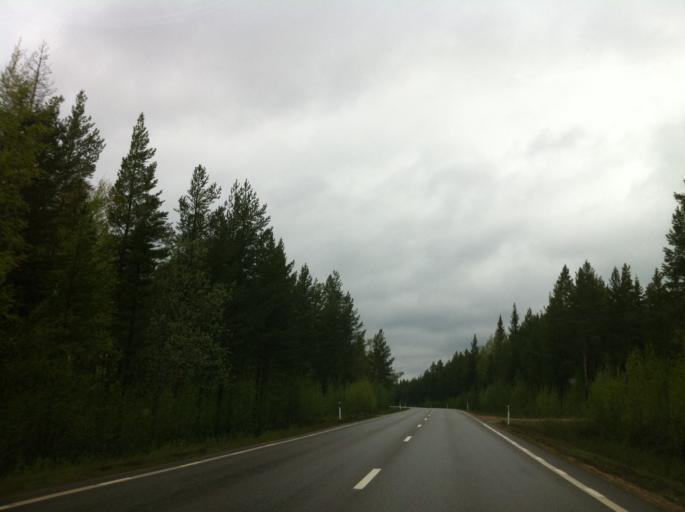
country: SE
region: Jaemtland
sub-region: Harjedalens Kommun
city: Sveg
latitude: 62.1039
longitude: 14.2050
